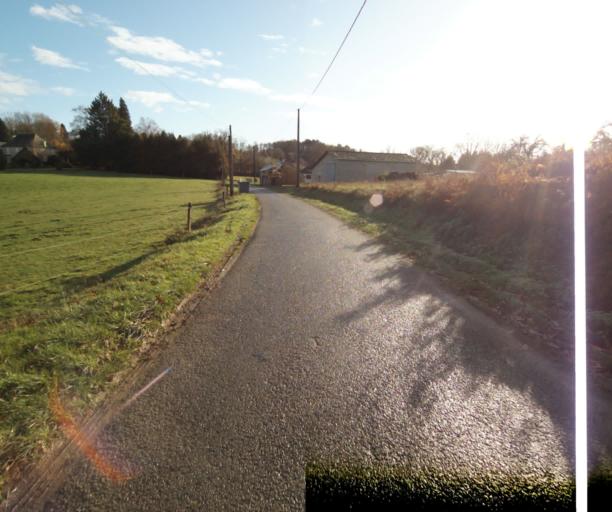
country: FR
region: Limousin
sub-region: Departement de la Correze
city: Saint-Mexant
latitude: 45.2503
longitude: 1.6218
